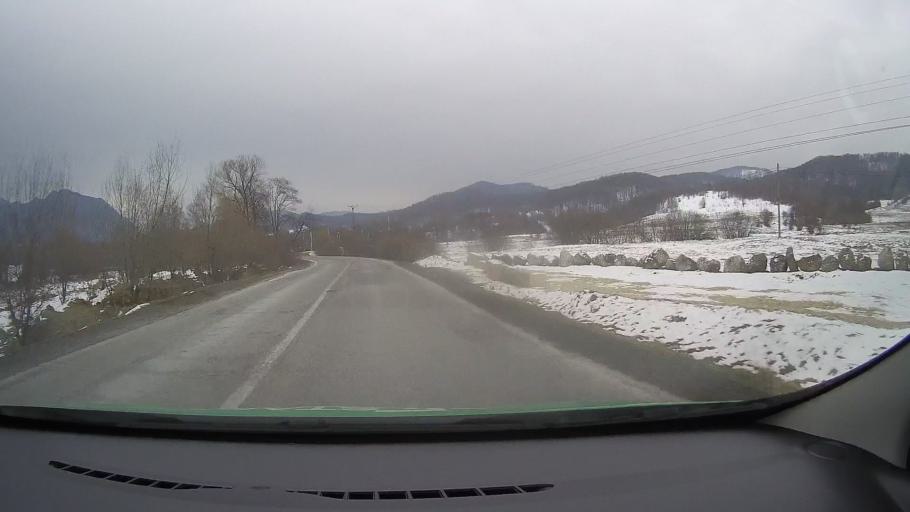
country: RO
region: Brasov
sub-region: Oras Rasnov
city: Rasnov
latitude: 45.5584
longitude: 25.4701
